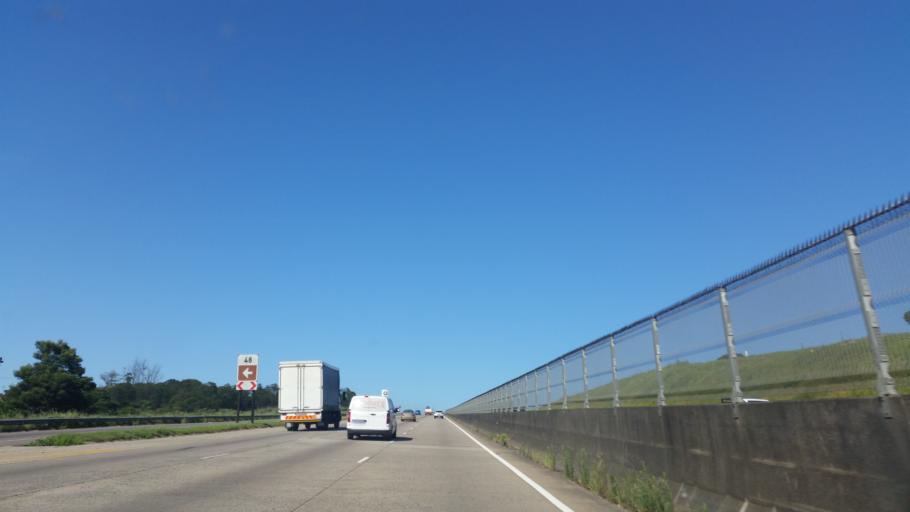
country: ZA
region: KwaZulu-Natal
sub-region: eThekwini Metropolitan Municipality
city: Mpumalanga
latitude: -29.7391
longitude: 30.6385
